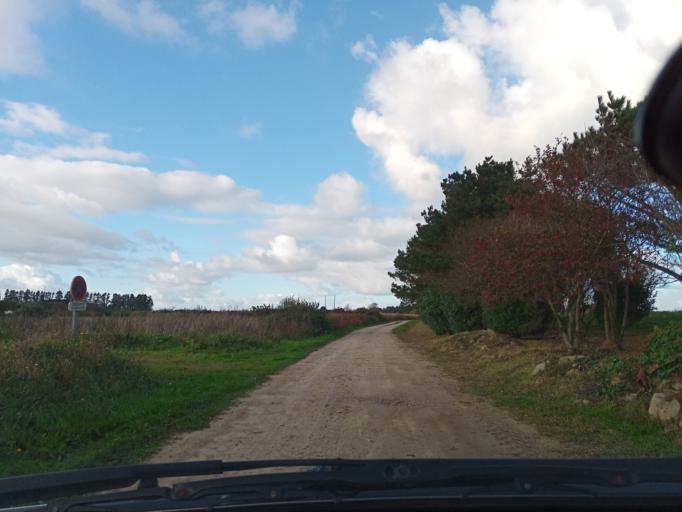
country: FR
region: Brittany
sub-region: Departement du Finistere
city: Plouhinec
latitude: 48.0177
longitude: -4.4928
